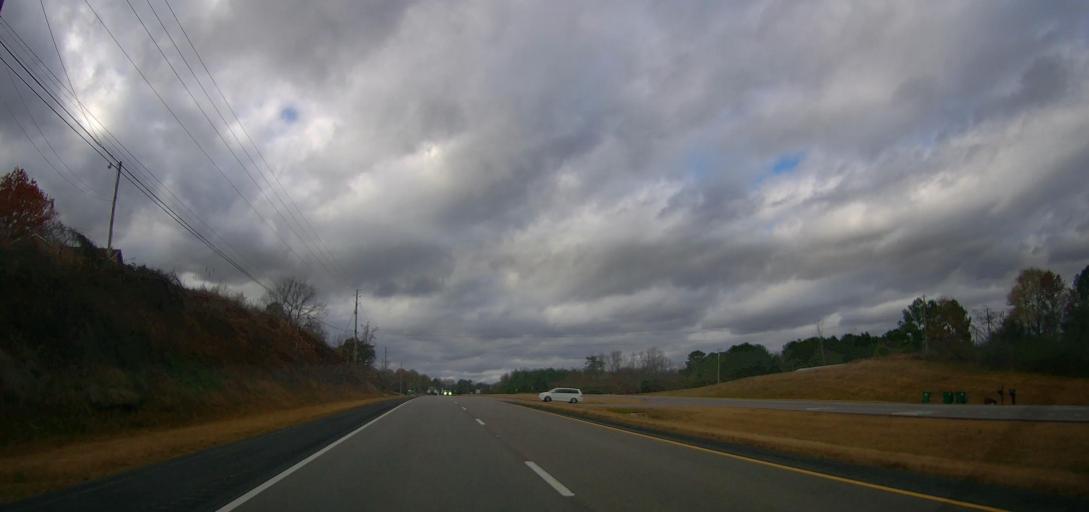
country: US
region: Alabama
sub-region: Morgan County
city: Falkville
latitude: 34.2595
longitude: -86.9822
